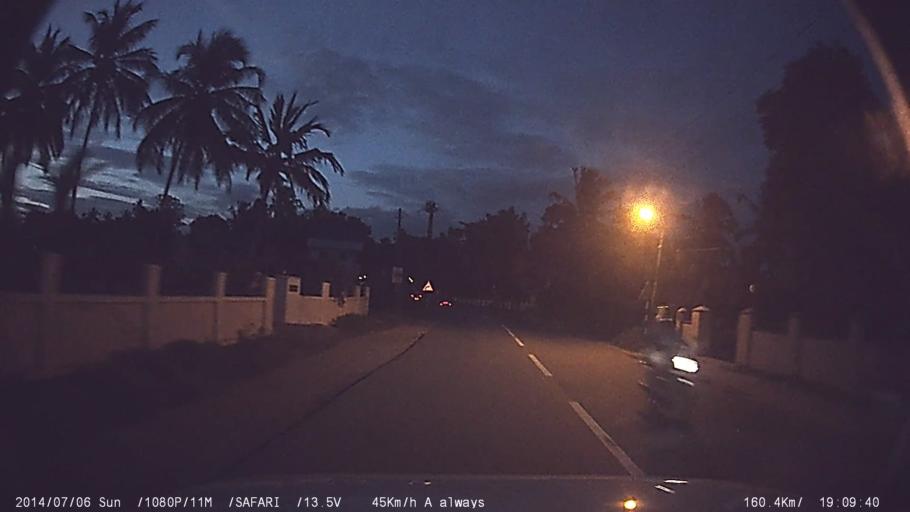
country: IN
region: Kerala
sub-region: Palakkad district
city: Palakkad
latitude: 10.7574
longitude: 76.6521
